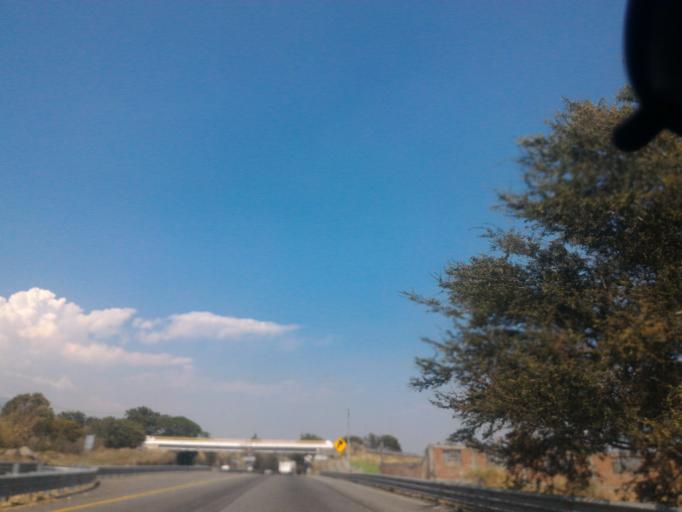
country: MX
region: Colima
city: Queseria
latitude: 19.3763
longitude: -103.5586
